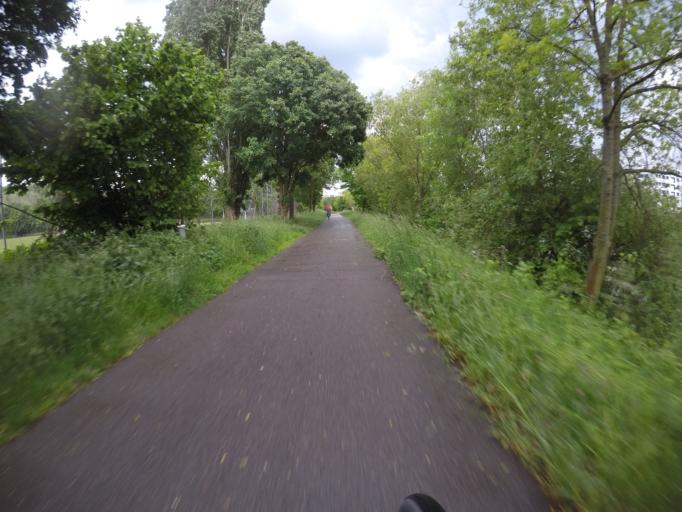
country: DE
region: Baden-Wuerttemberg
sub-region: Regierungsbezirk Stuttgart
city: Ostfildern
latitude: 48.7439
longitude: 9.2735
